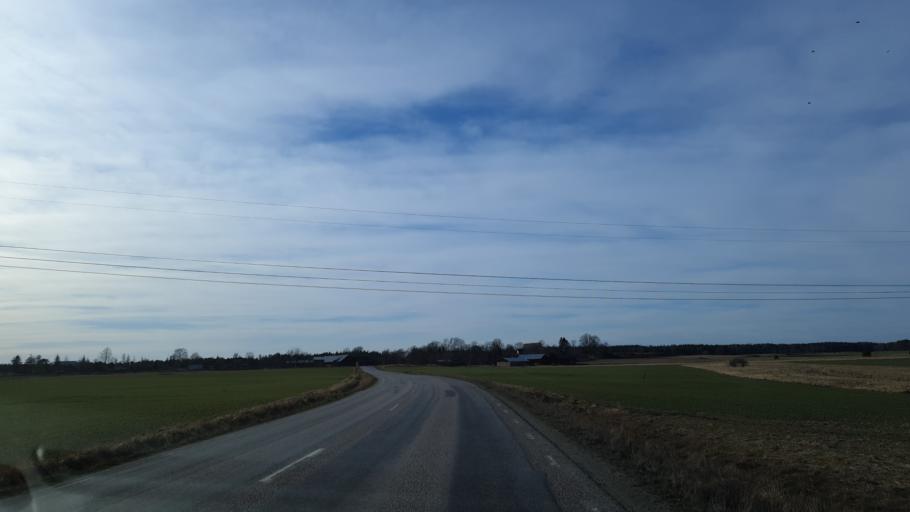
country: SE
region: Uppsala
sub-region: Enkopings Kommun
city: Grillby
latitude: 59.5931
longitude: 17.1899
